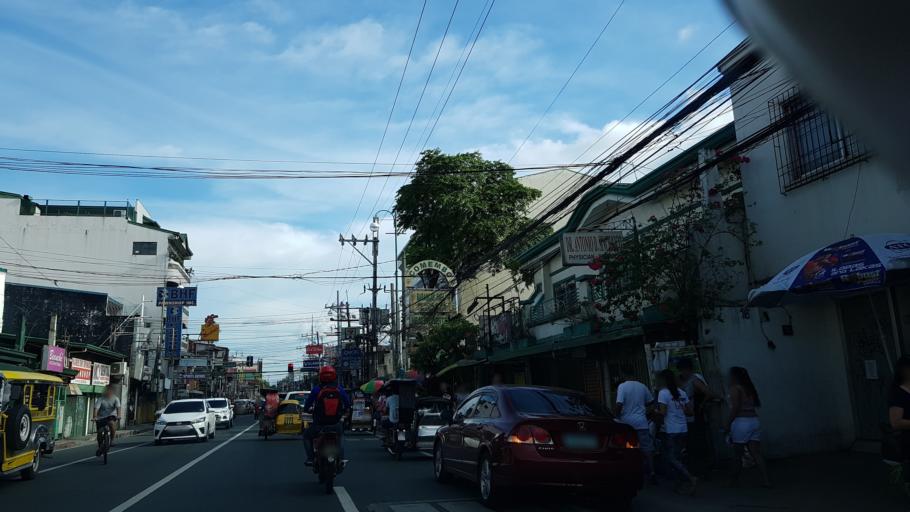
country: PH
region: Calabarzon
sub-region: Province of Rizal
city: Pateros
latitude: 14.5494
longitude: 121.0637
